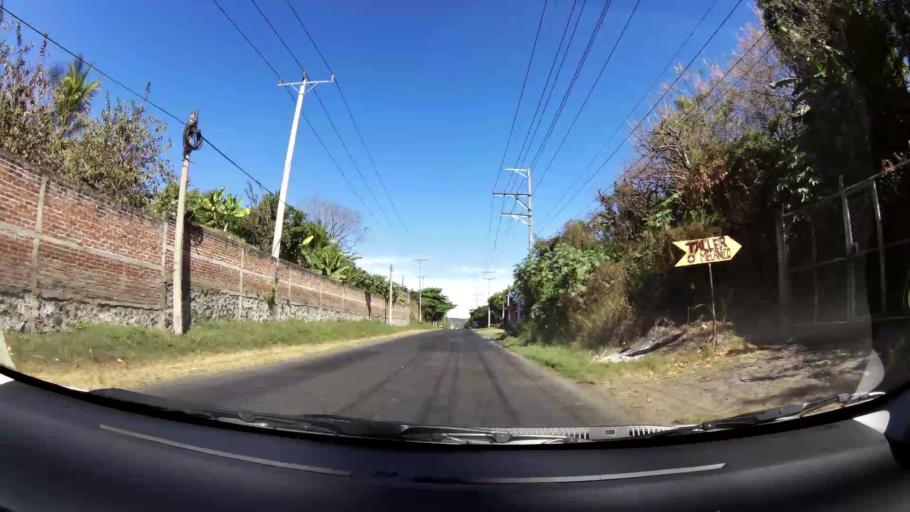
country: SV
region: La Libertad
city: San Juan Opico
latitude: 13.8345
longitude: -89.3588
